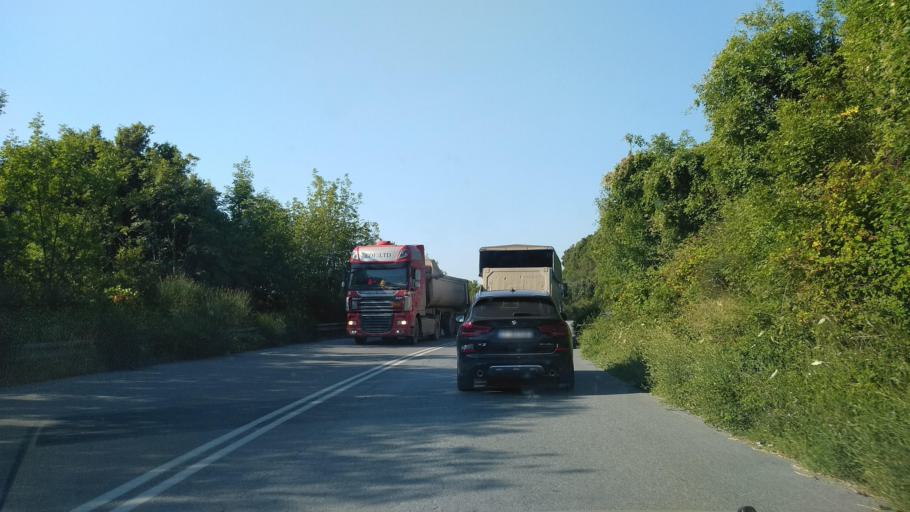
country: GR
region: Central Macedonia
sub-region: Nomos Chalkidikis
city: Stratonion
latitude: 40.5253
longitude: 23.8248
